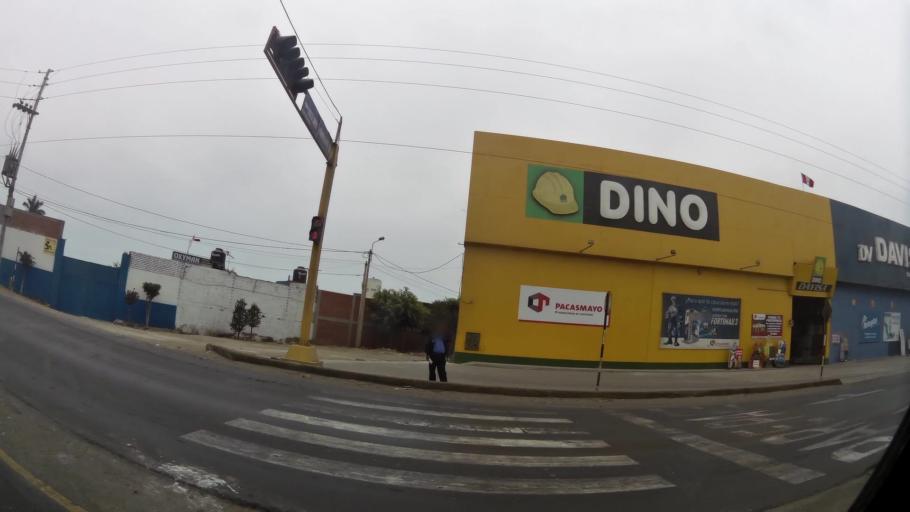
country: PE
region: La Libertad
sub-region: Provincia de Trujillo
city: Moche
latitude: -8.1489
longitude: -79.0117
